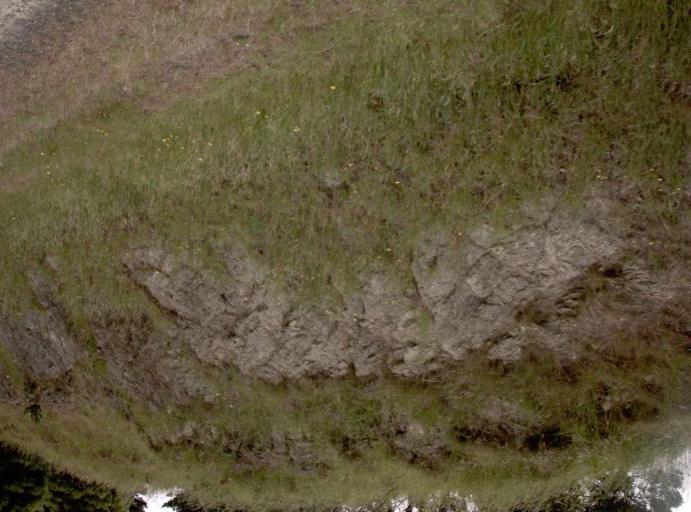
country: AU
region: Victoria
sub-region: Latrobe
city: Morwell
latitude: -38.6369
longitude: 146.2013
